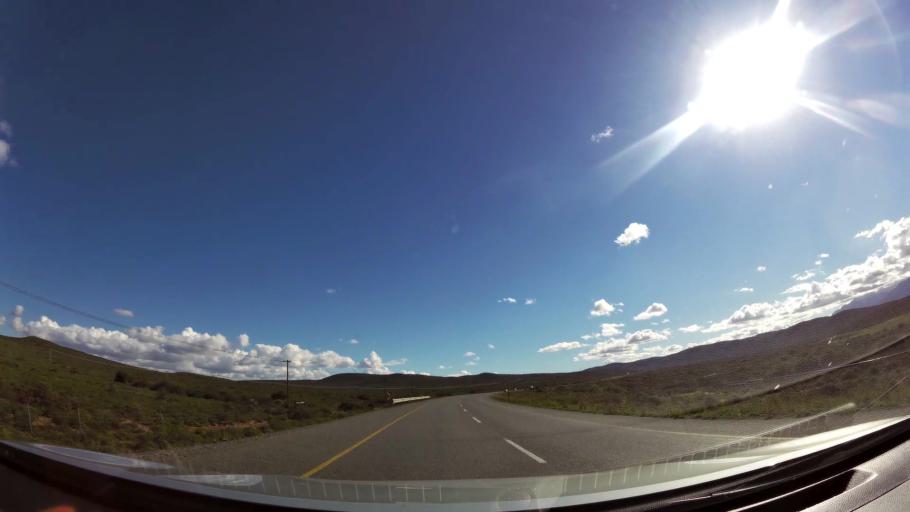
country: ZA
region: Western Cape
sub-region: Cape Winelands District Municipality
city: Worcester
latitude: -33.7505
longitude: 19.7111
